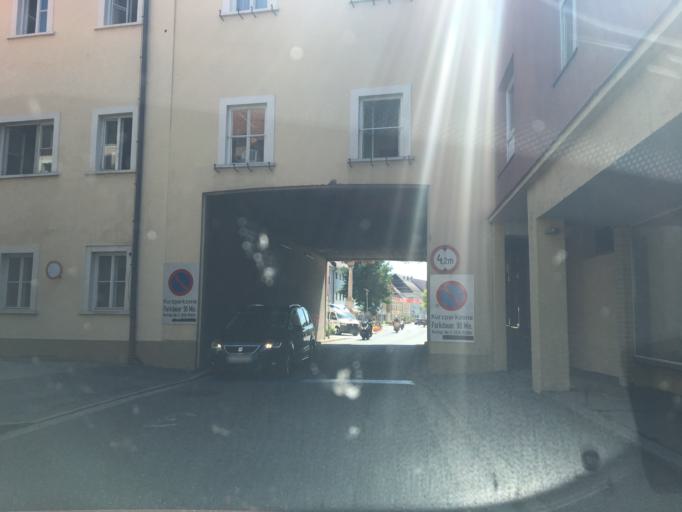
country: AT
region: Carinthia
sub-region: Politischer Bezirk Volkermarkt
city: Voelkermarkt
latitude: 46.6609
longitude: 14.6338
